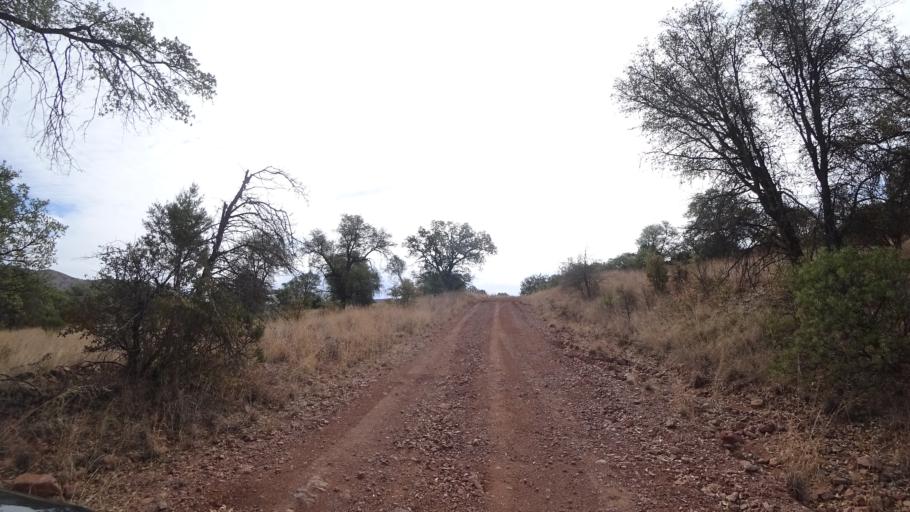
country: MX
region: Sonora
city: Santa Cruz
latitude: 31.4834
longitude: -110.5700
